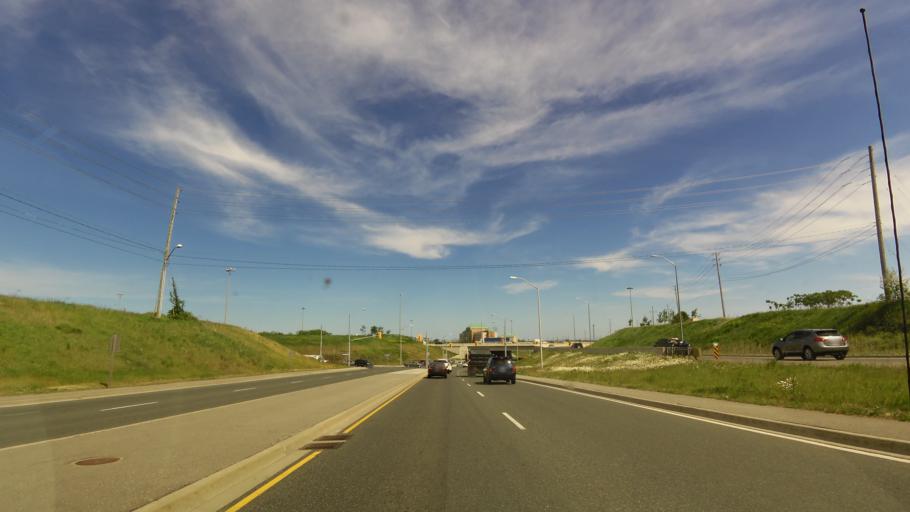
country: CA
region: Ontario
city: Oakville
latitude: 43.4117
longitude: -79.7427
